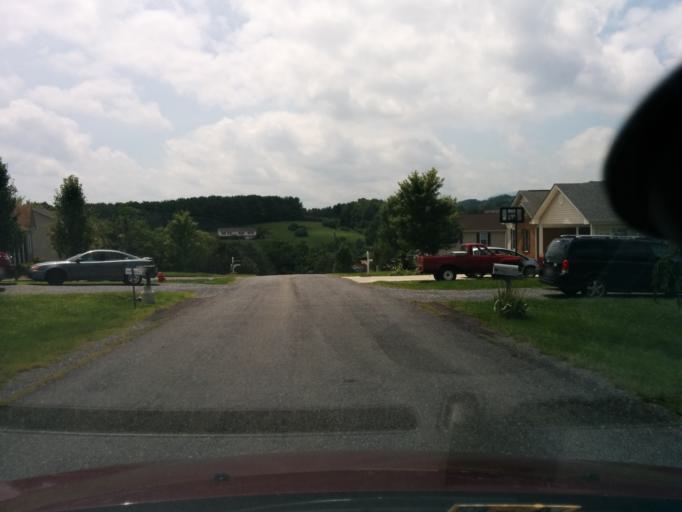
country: US
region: Virginia
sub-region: Rockbridge County
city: East Lexington
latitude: 37.8246
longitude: -79.3986
